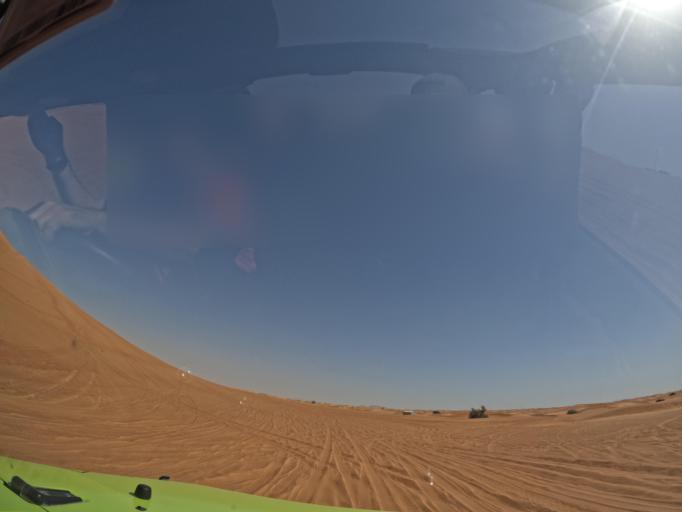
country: AE
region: Ash Shariqah
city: Adh Dhayd
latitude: 24.9580
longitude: 55.7194
